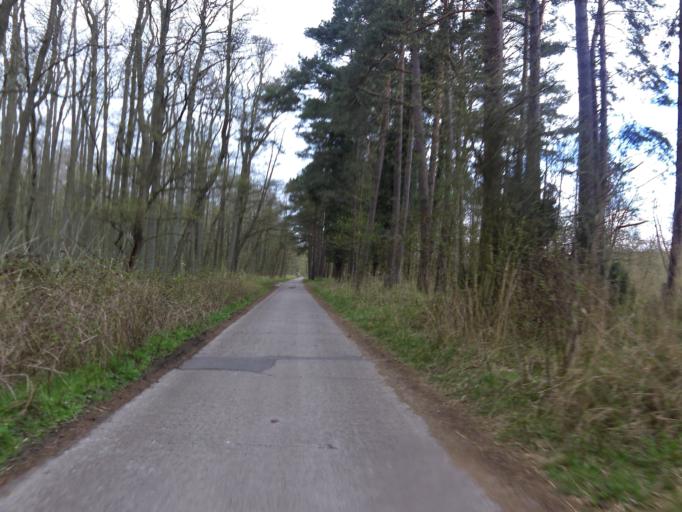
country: DE
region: Mecklenburg-Vorpommern
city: Ostseebad Prerow
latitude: 54.4645
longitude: 12.5260
